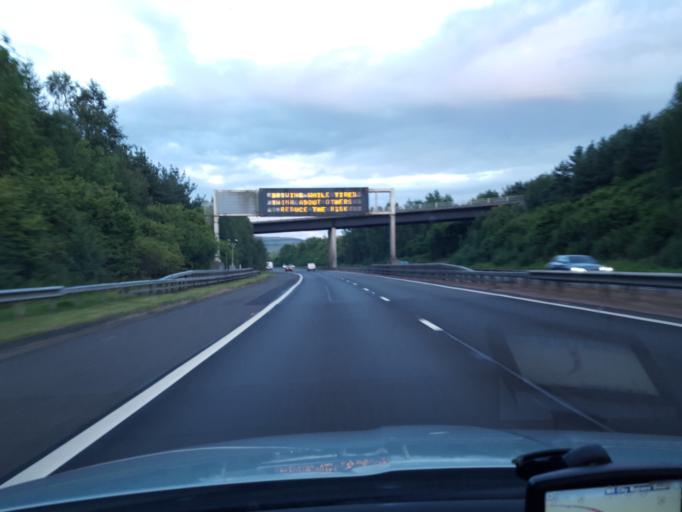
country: GB
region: Scotland
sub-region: Edinburgh
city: Ratho
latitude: 55.9221
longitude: -3.3432
